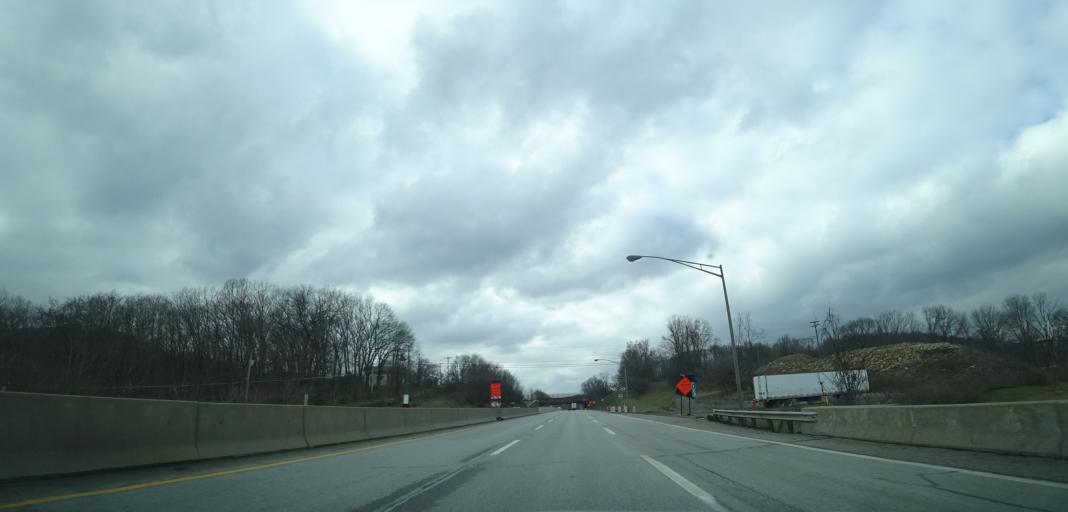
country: US
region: Pennsylvania
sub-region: Beaver County
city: West Mayfield
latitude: 40.8140
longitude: -80.3247
